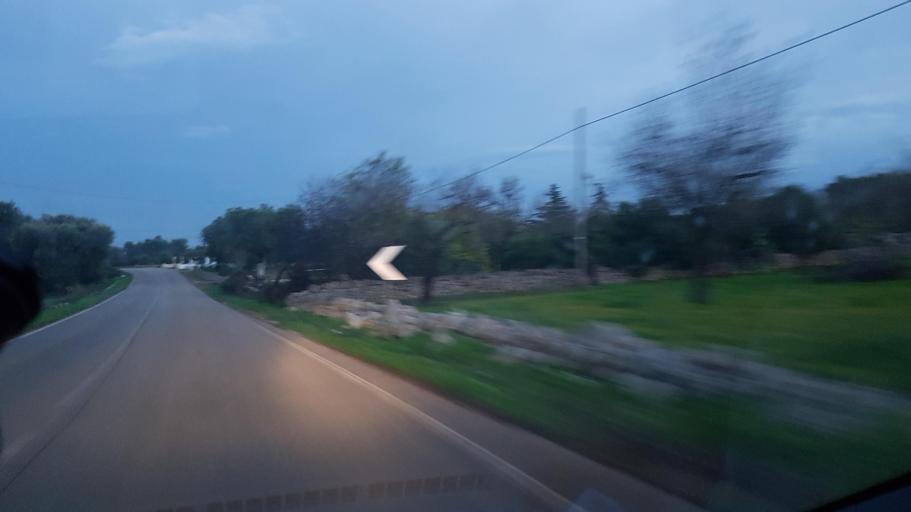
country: IT
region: Apulia
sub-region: Provincia di Brindisi
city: San Vito dei Normanni
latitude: 40.6485
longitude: 17.6836
